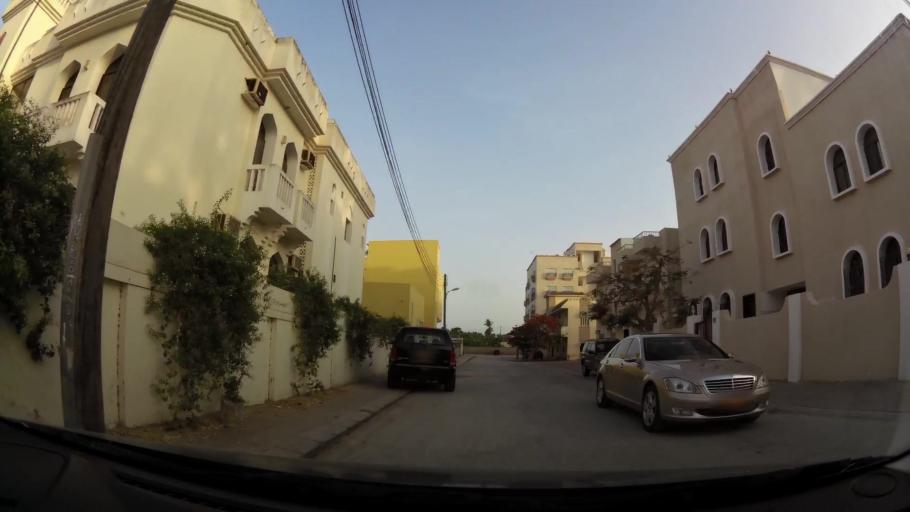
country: OM
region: Zufar
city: Salalah
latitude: 17.0152
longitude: 54.1144
